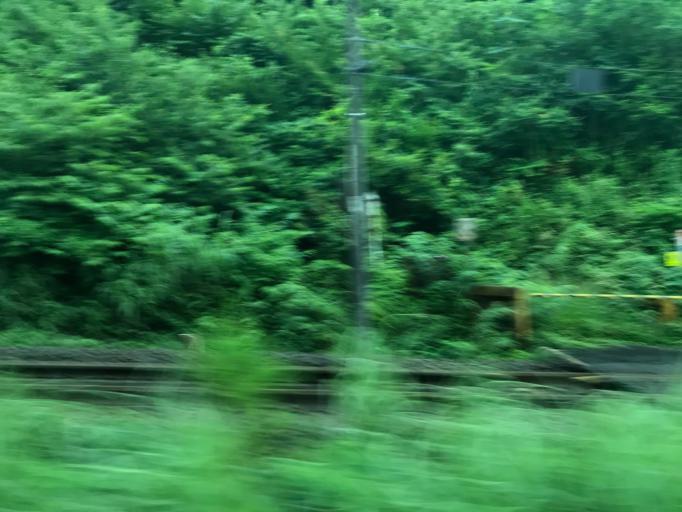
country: JP
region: Tochigi
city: Kuroiso
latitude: 37.0795
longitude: 140.1711
